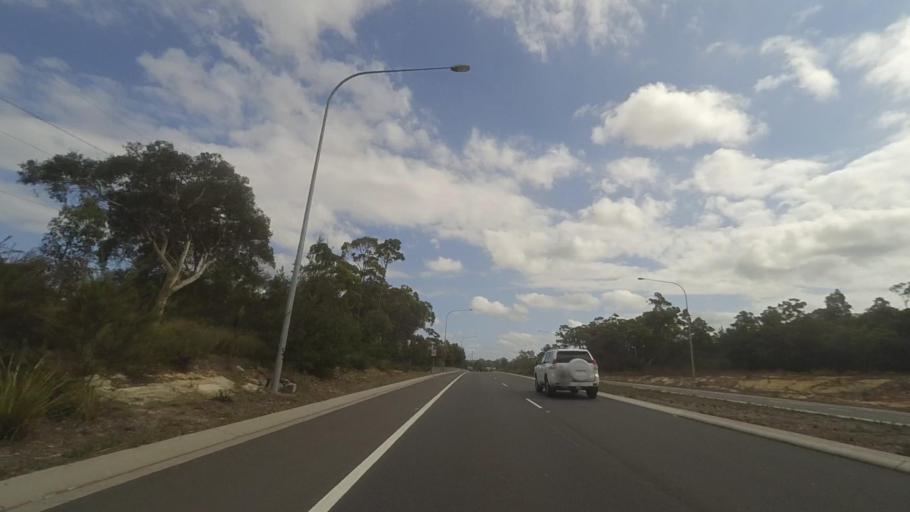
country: AU
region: New South Wales
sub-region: Sutherland Shire
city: Menai
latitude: -34.0289
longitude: 151.0064
